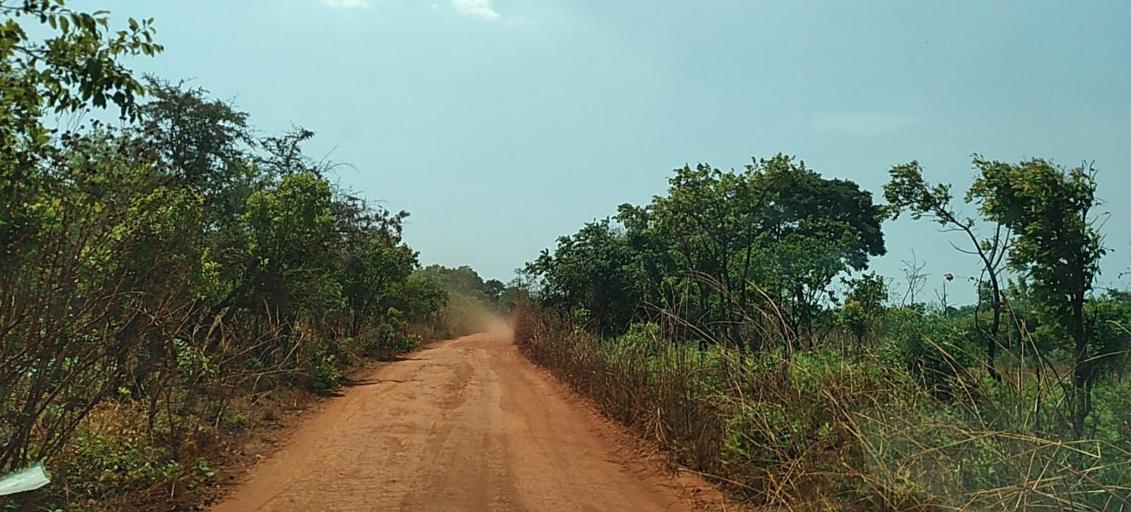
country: ZM
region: North-Western
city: Solwezi
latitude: -12.1290
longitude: 26.3108
